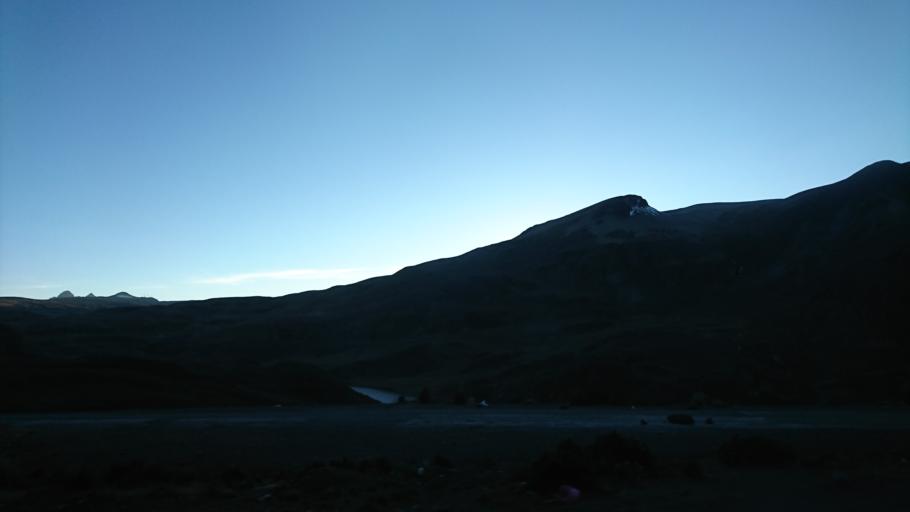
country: BO
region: La Paz
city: La Paz
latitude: -16.3829
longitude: -68.0419
